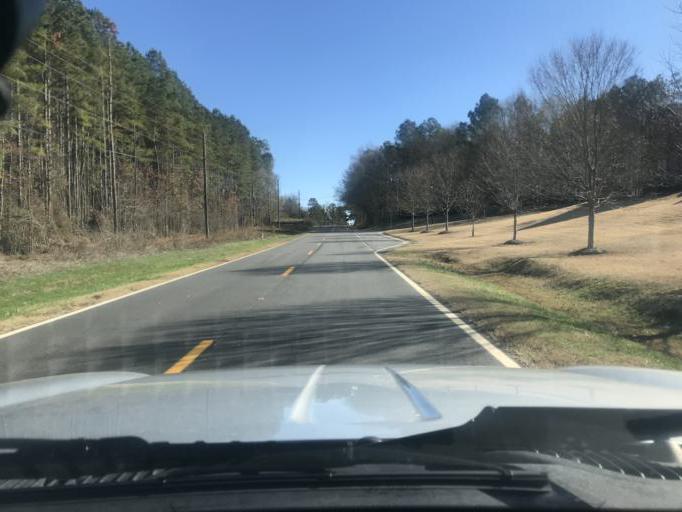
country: US
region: Georgia
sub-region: Barrow County
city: Russell
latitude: 33.9094
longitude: -83.7461
